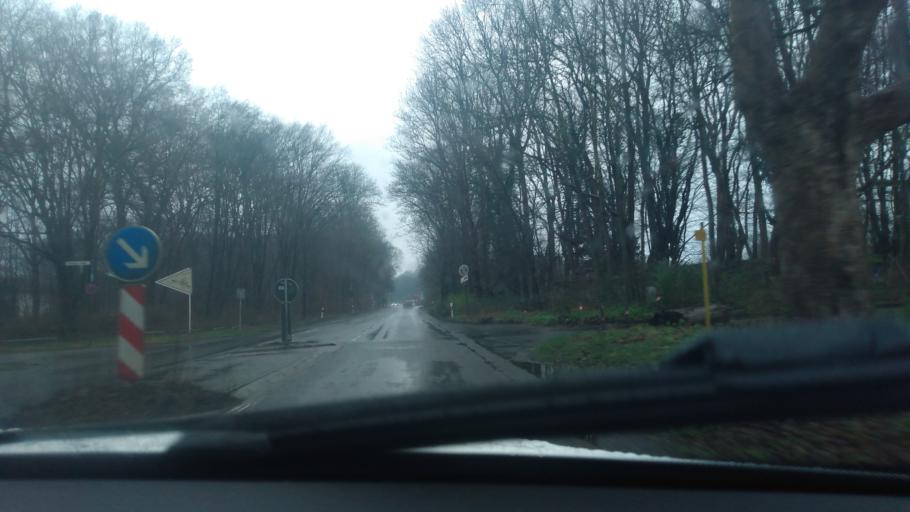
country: DE
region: North Rhine-Westphalia
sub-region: Regierungsbezirk Koln
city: Hurth
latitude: 50.9200
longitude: 6.8914
